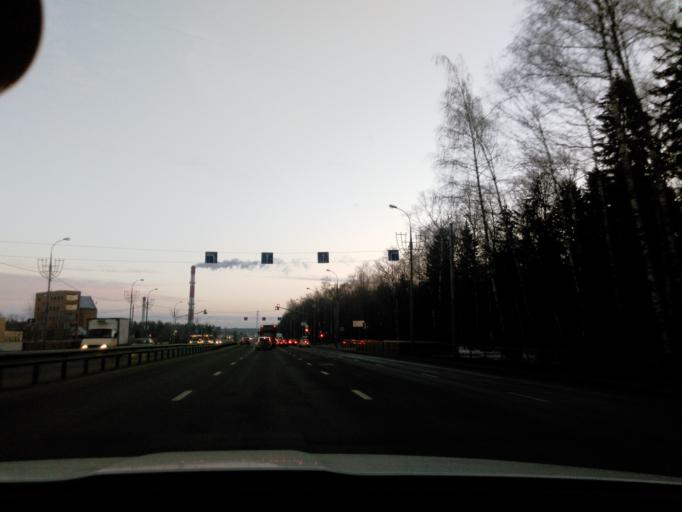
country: RU
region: Moscow
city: Zelenograd
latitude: 55.9983
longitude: 37.1925
